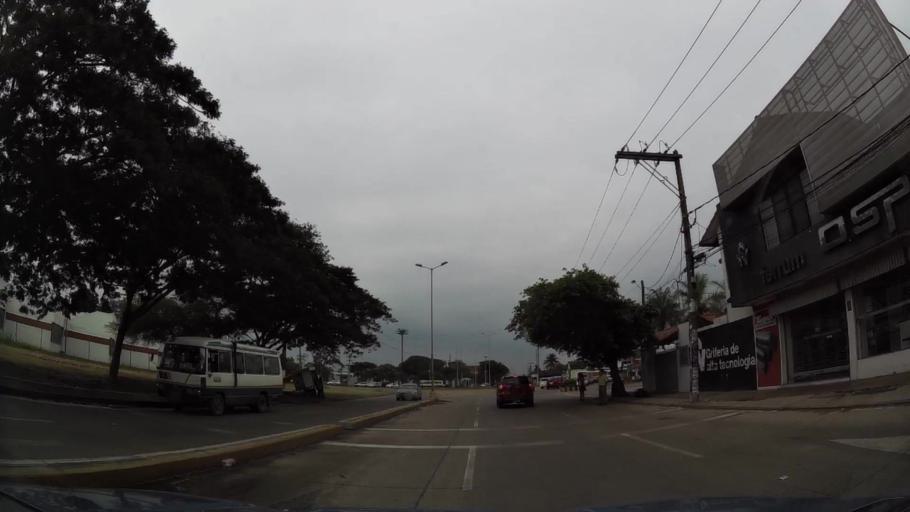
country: BO
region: Santa Cruz
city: Santa Cruz de la Sierra
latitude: -17.7695
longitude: -63.1574
